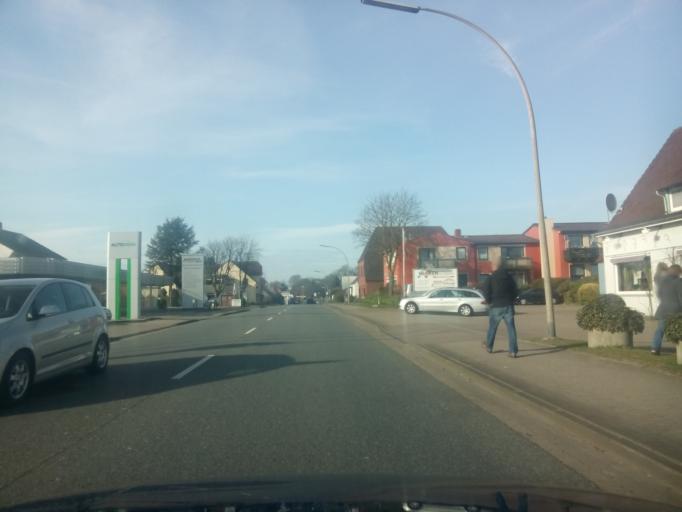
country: DE
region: Lower Saxony
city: Ritterhude
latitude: 53.1999
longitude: 8.7554
